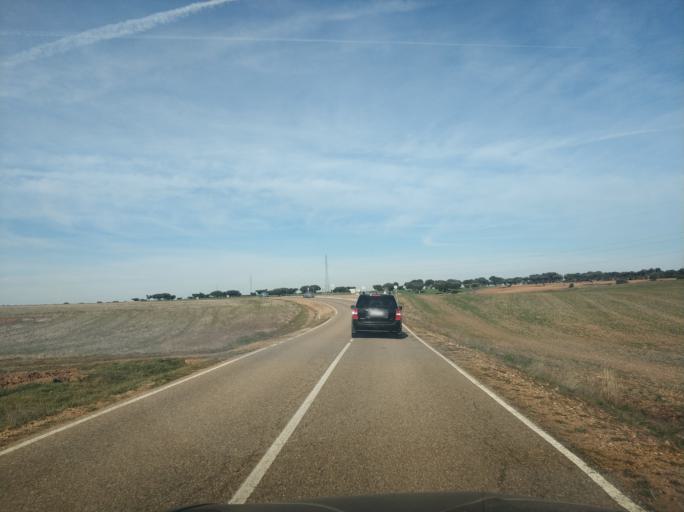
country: ES
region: Castille and Leon
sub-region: Provincia de Salamanca
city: Parada de Arriba
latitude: 40.9942
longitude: -5.8087
